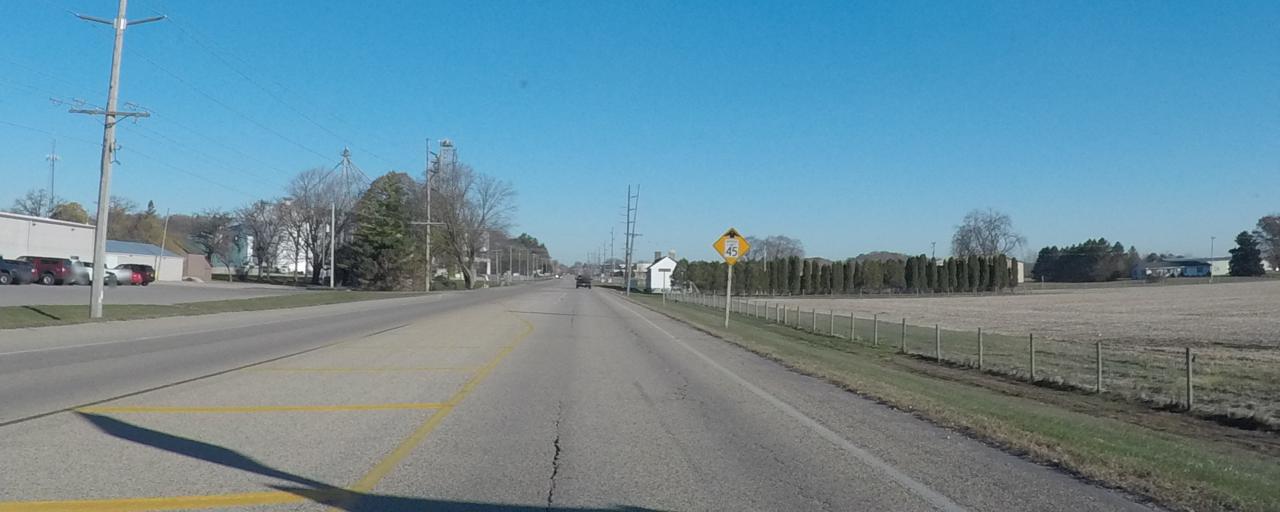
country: US
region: Wisconsin
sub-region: Dane County
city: Cottage Grove
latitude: 43.0629
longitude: -89.1997
